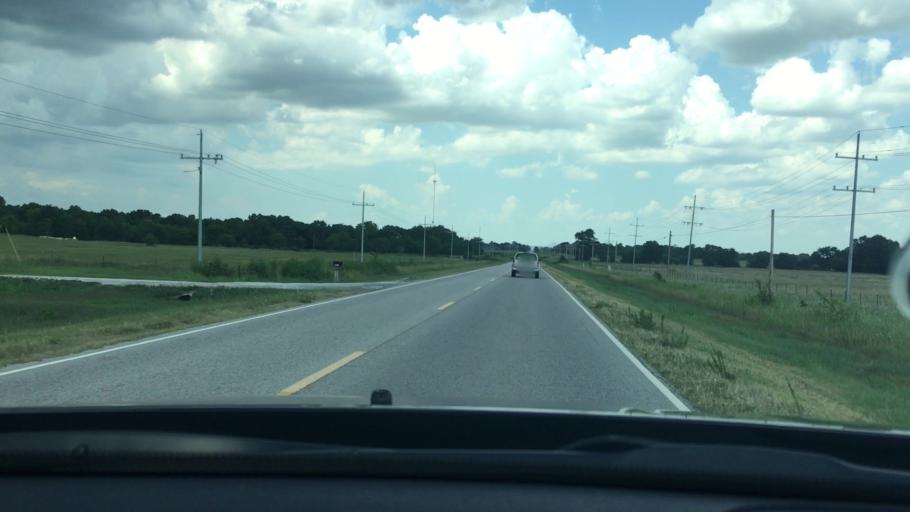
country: US
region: Oklahoma
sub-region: Pontotoc County
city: Ada
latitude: 34.6421
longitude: -96.6348
